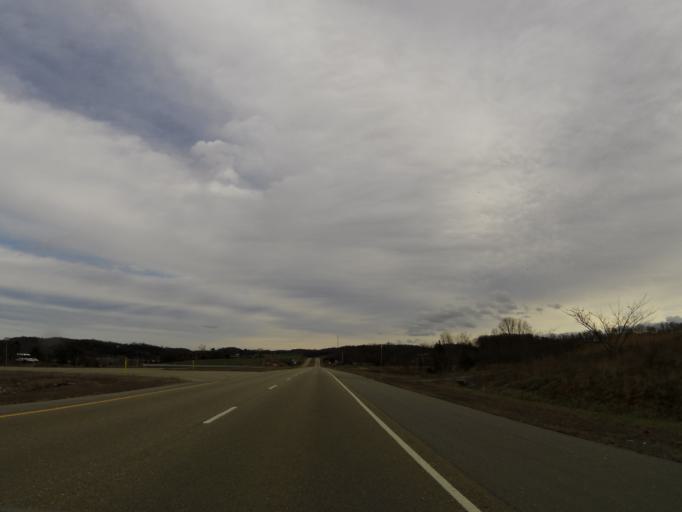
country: US
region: Tennessee
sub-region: Cocke County
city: Newport
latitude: 36.0111
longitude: -83.0586
